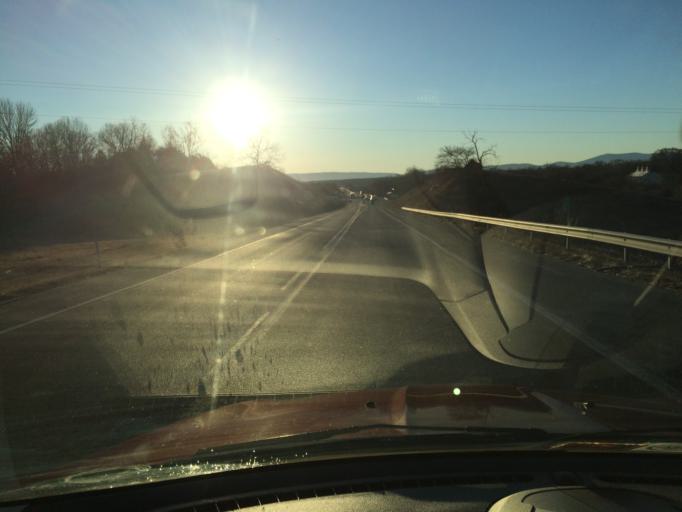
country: US
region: Virginia
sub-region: Augusta County
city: Verona
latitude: 38.1841
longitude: -79.0362
